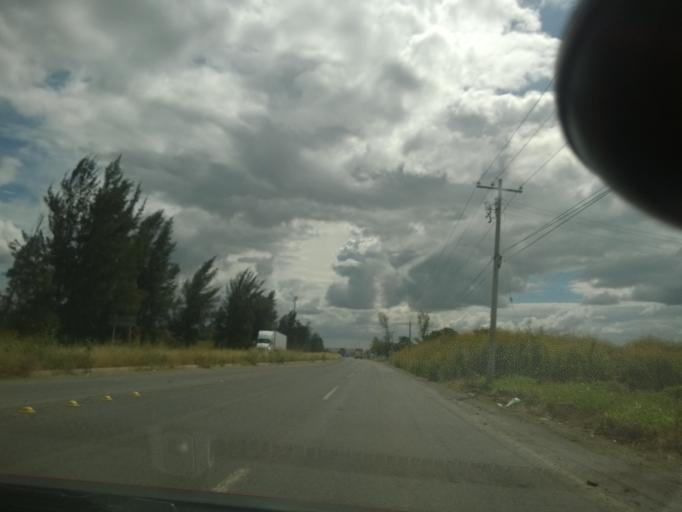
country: MX
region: Guanajuato
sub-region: Leon
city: El CERESO
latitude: 21.0231
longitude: -101.6978
